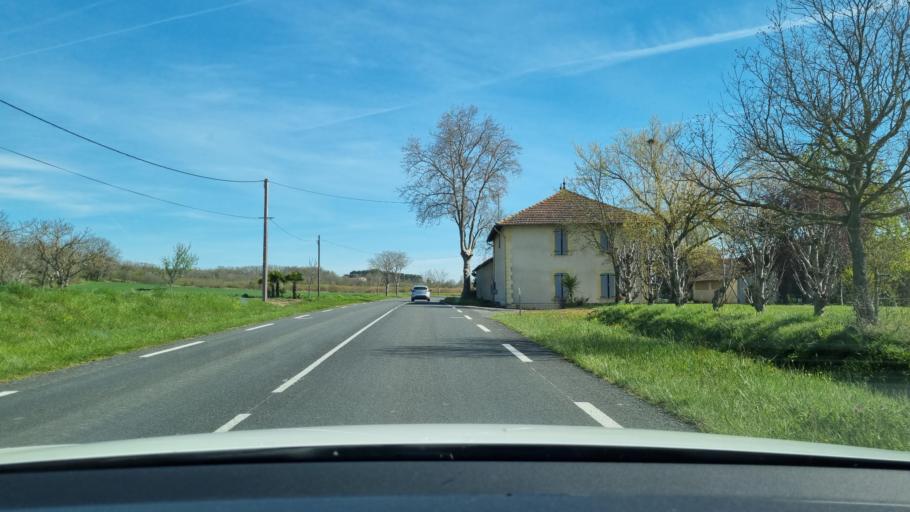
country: FR
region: Midi-Pyrenees
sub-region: Departement du Gers
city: Lombez
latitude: 43.3933
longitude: 0.7860
